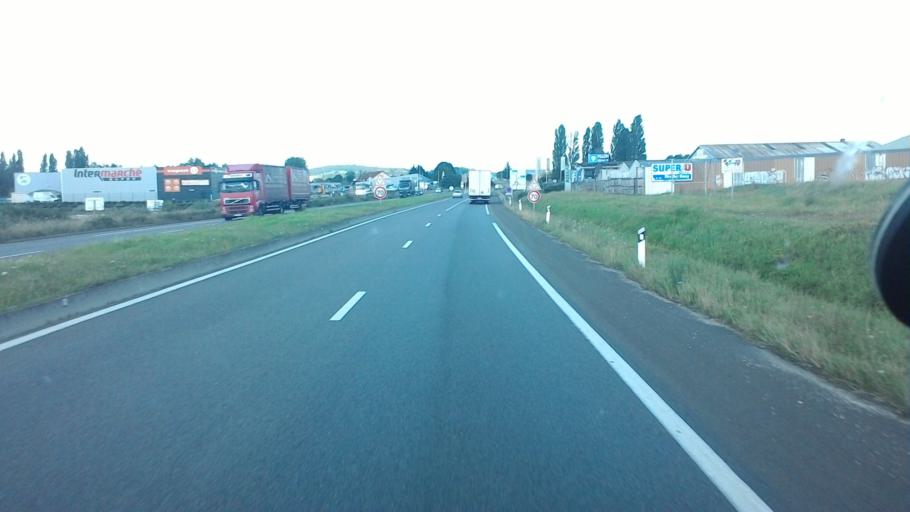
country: FR
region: Franche-Comte
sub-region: Departement de la Haute-Saone
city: Pusey
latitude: 47.6393
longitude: 6.1402
